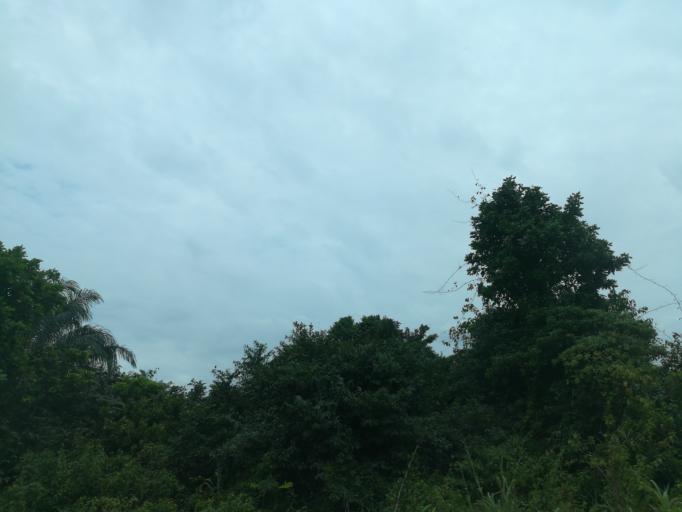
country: NG
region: Lagos
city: Ejirin
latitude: 6.6491
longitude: 3.8300
